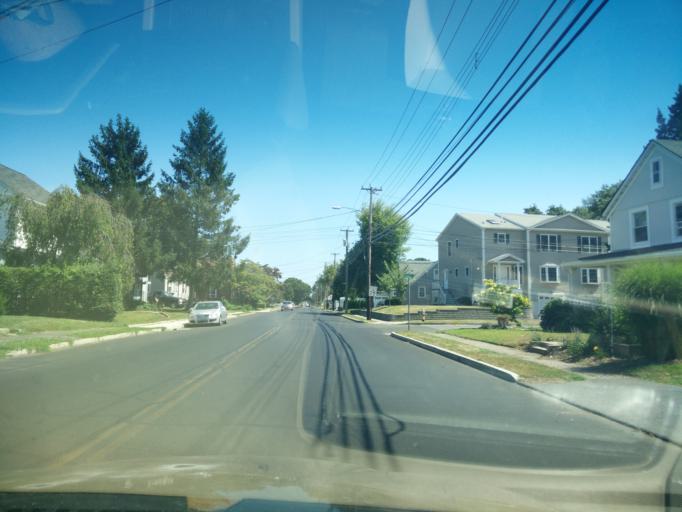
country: US
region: Connecticut
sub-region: Fairfield County
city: Fairfield
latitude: 41.1352
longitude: -73.2529
